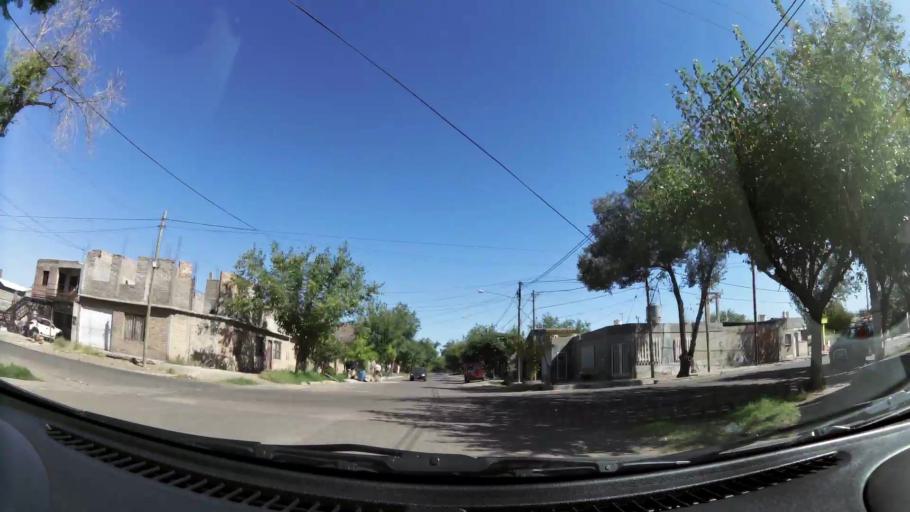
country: AR
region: Mendoza
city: Mendoza
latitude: -32.8816
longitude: -68.8046
